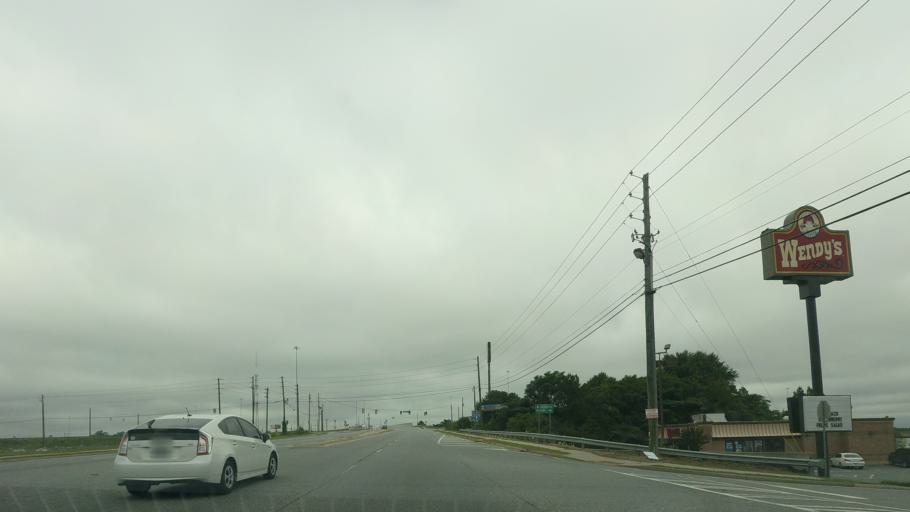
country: US
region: Georgia
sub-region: Peach County
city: Byron
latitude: 32.7435
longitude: -83.7151
